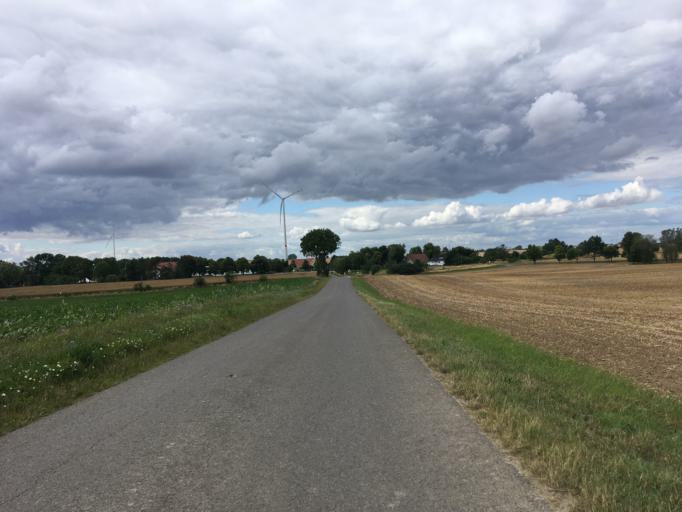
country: DE
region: Brandenburg
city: Gramzow
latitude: 53.2678
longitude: 14.0134
